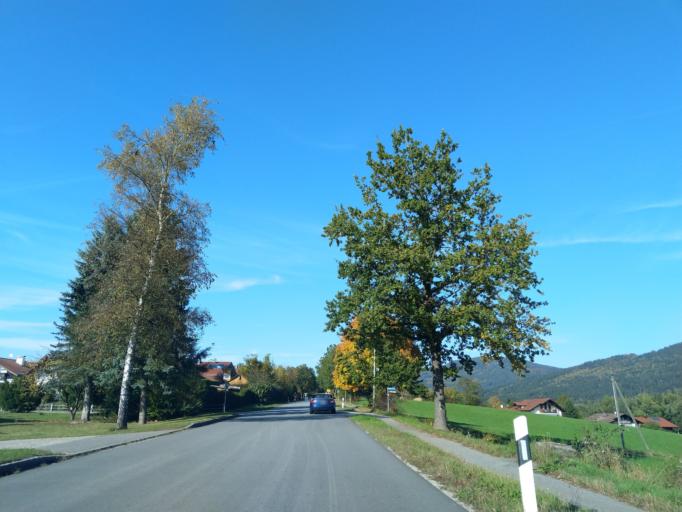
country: DE
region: Bavaria
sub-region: Lower Bavaria
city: Metten
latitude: 48.8855
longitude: 12.9249
